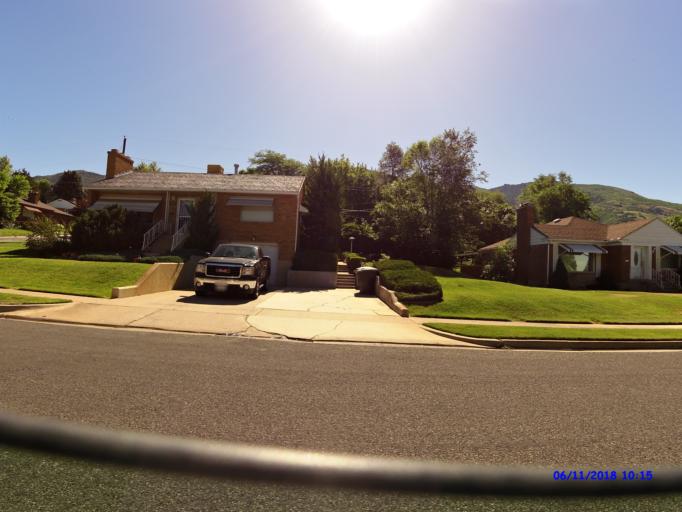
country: US
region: Utah
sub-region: Weber County
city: South Ogden
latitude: 41.2086
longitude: -111.9453
